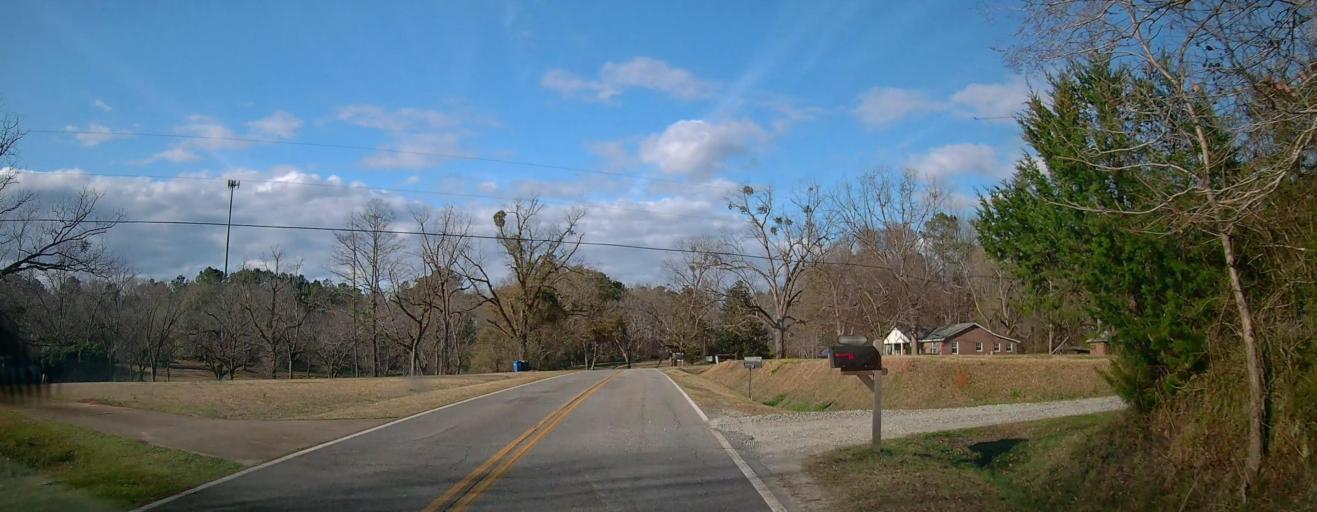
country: US
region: Georgia
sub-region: Harris County
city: Hamilton
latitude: 32.5556
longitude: -84.7797
